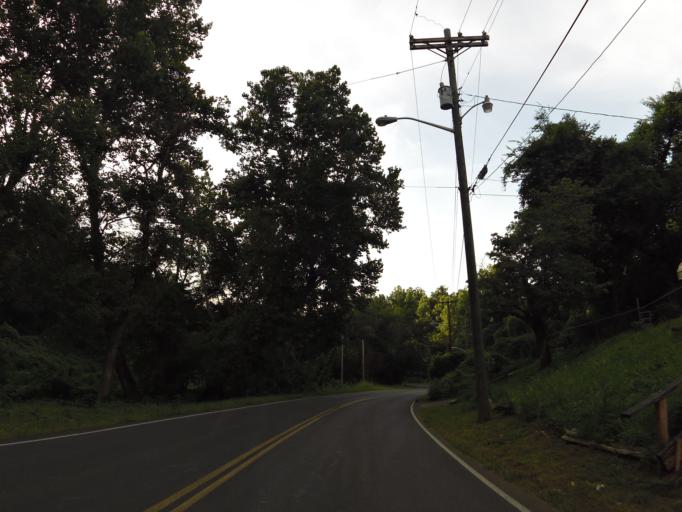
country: US
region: Tennessee
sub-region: Knox County
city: Knoxville
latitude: 35.9398
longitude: -83.9164
